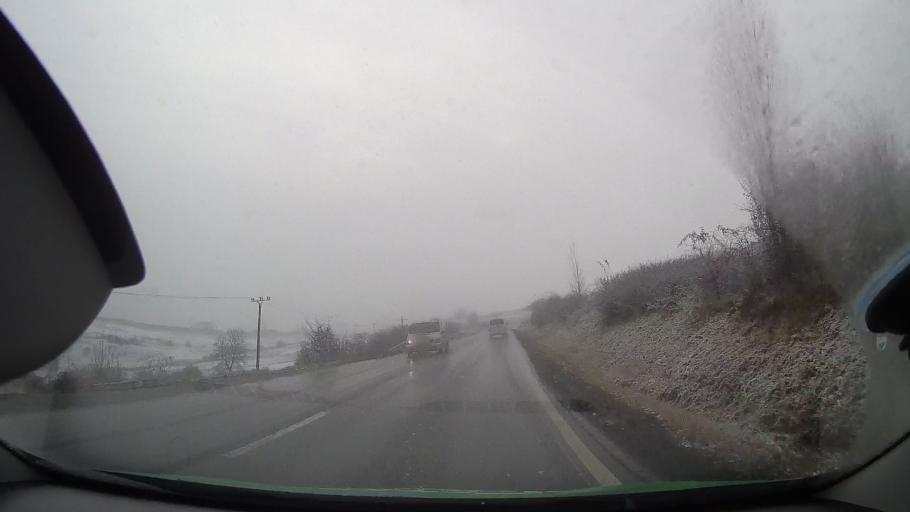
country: RO
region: Mures
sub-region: Comuna Bagaciu
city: Delenii
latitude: 46.2601
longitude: 24.3009
